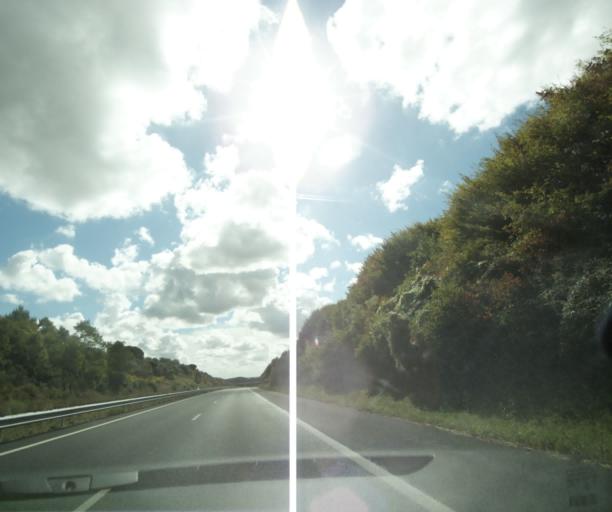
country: FR
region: Poitou-Charentes
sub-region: Departement de la Charente-Maritime
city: Bords
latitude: 45.9005
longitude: -0.7601
